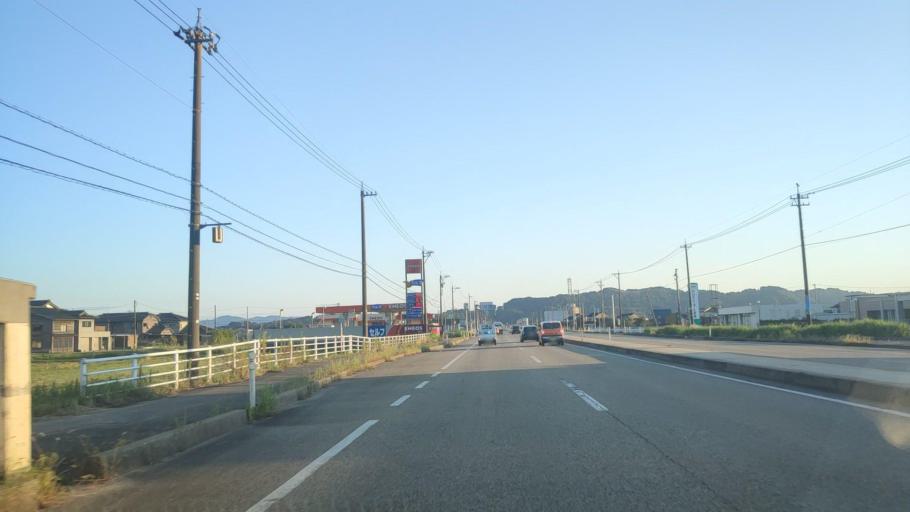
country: JP
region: Toyama
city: Himi
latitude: 36.8715
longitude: 136.9753
